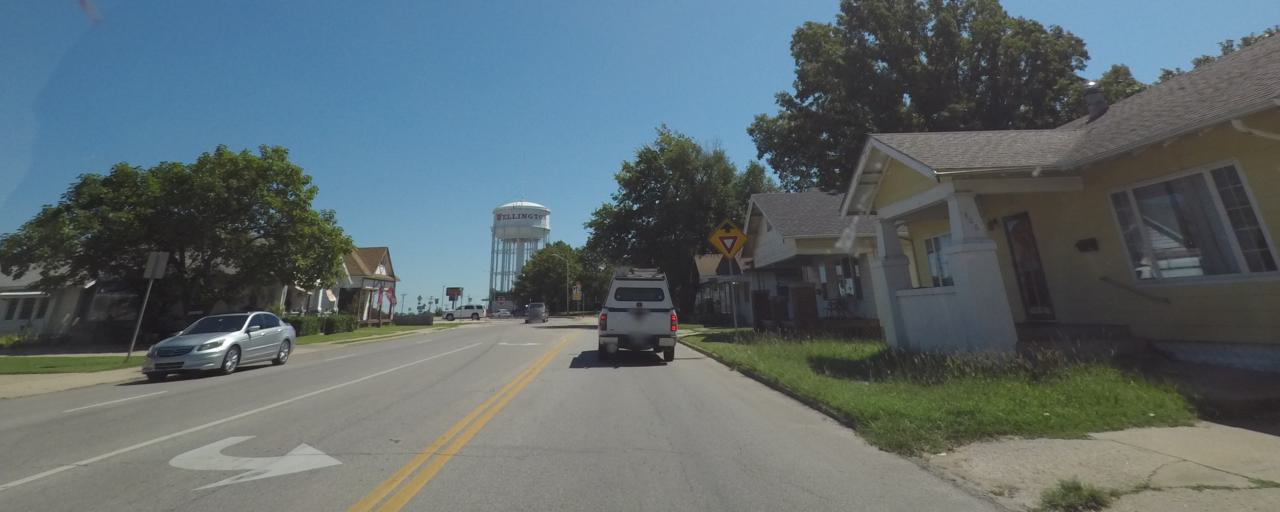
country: US
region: Kansas
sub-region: Sumner County
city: Wellington
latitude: 37.2745
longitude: -97.3955
